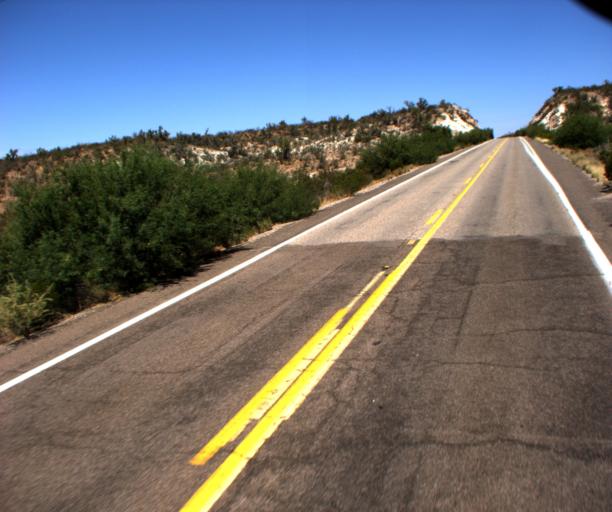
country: US
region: Arizona
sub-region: Gila County
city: Peridot
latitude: 33.2511
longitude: -110.2759
